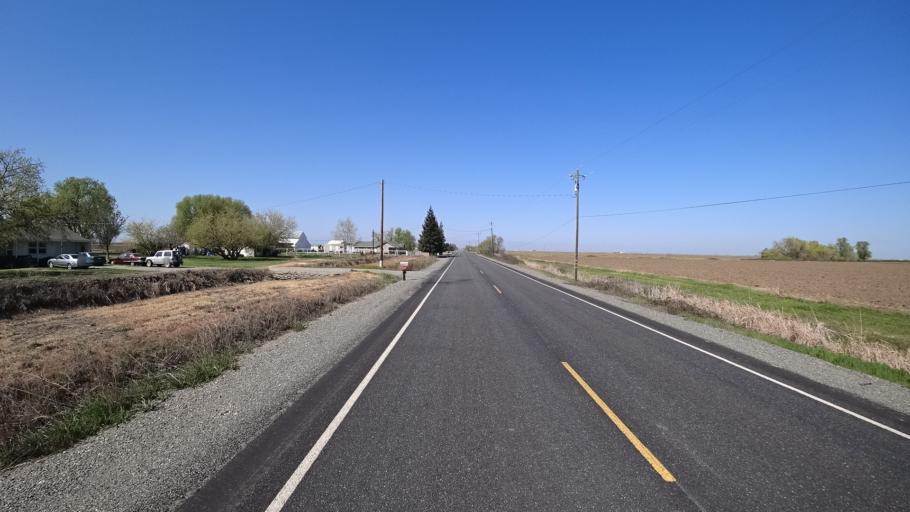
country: US
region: California
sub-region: Glenn County
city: Willows
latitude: 39.4576
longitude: -122.0397
